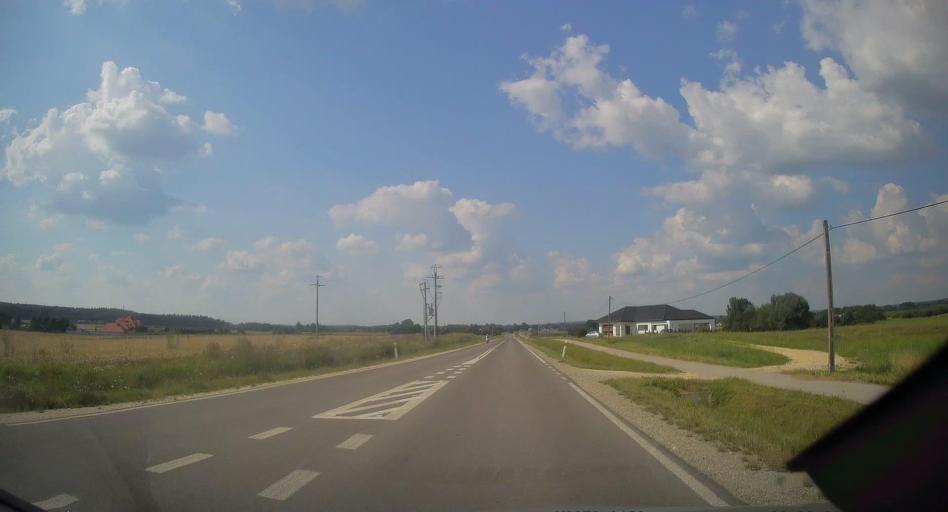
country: PL
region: Swietokrzyskie
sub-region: Powiat kielecki
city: Lopuszno
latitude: 50.9559
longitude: 20.2501
